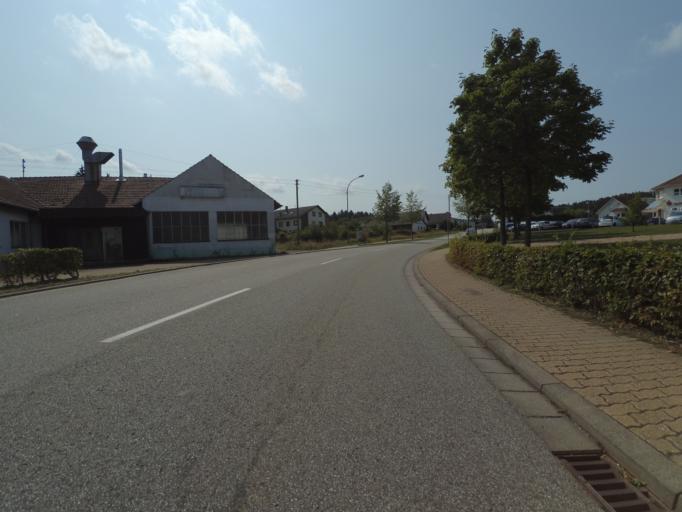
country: DE
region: Saarland
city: Britten
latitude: 49.5225
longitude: 6.6714
